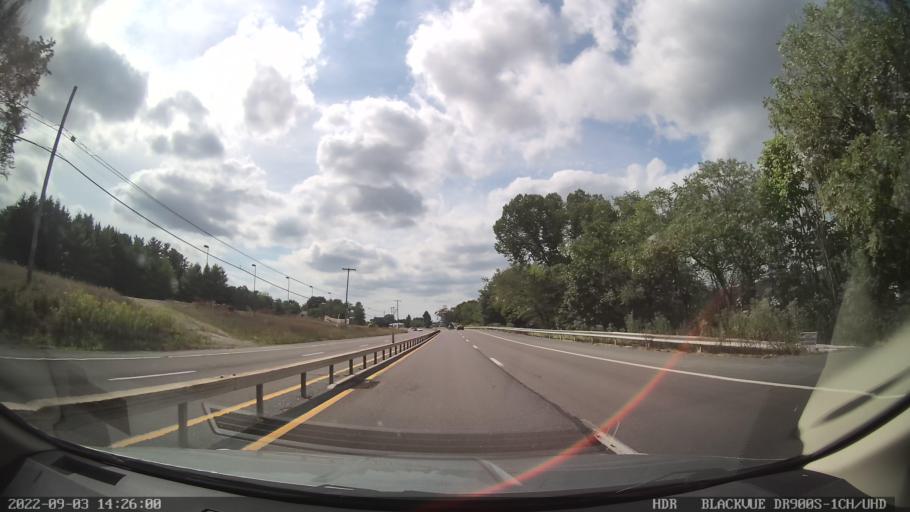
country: US
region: Pennsylvania
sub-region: Carbon County
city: Weissport East
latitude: 40.8379
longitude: -75.6815
